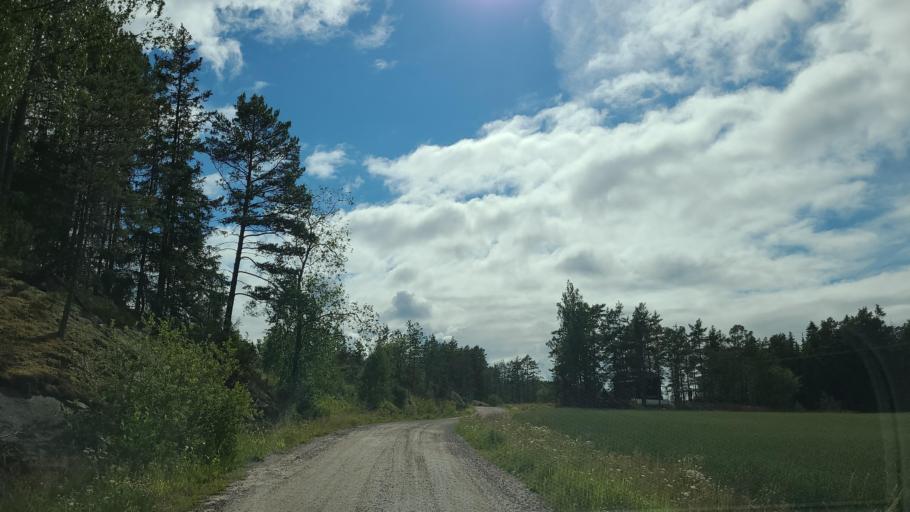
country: FI
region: Varsinais-Suomi
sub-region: Aboland-Turunmaa
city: Nagu
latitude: 60.1992
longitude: 21.7813
